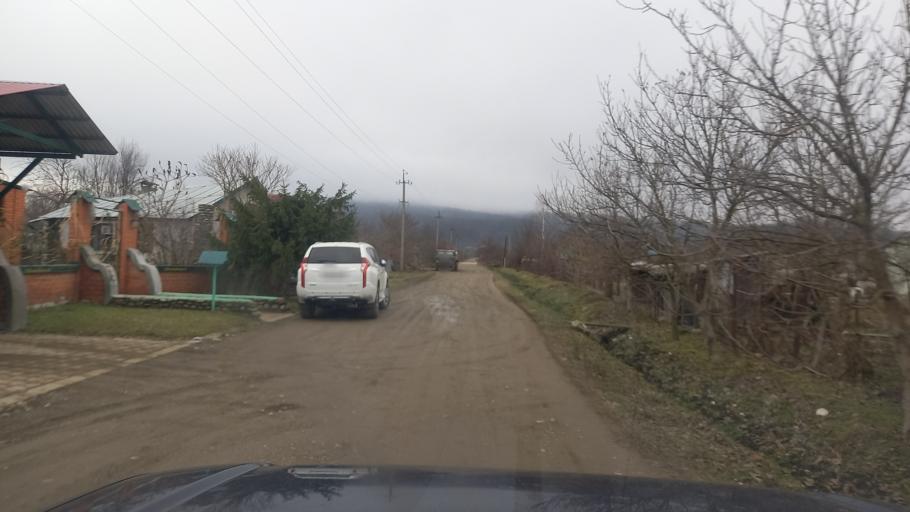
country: RU
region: Krasnodarskiy
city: Neftegorsk
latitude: 44.2492
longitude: 39.7647
